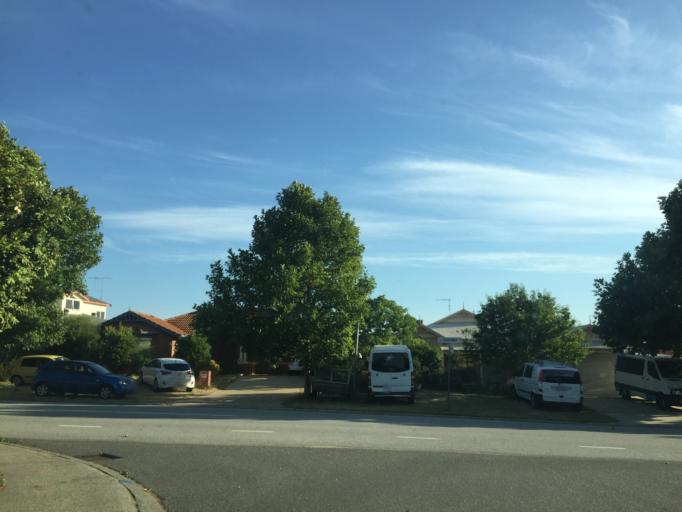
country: AU
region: Western Australia
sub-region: City of Cockburn
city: City of Cockburn
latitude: -32.0926
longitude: 115.8419
